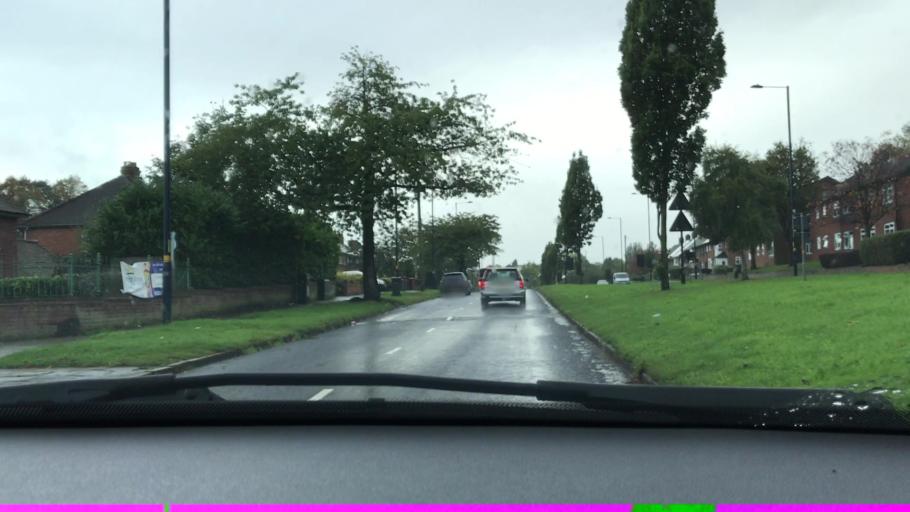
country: GB
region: England
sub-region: City and Borough of Birmingham
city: Bartley Green
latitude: 52.4605
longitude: -1.9767
